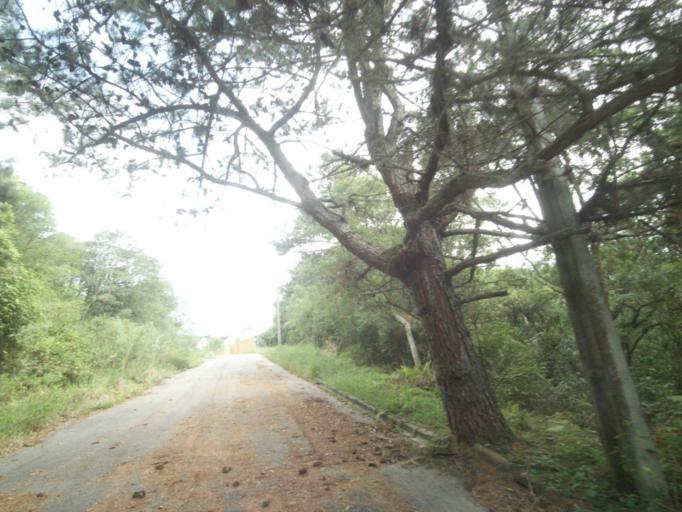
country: BR
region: Parana
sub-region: Curitiba
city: Curitiba
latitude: -25.3795
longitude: -49.2885
